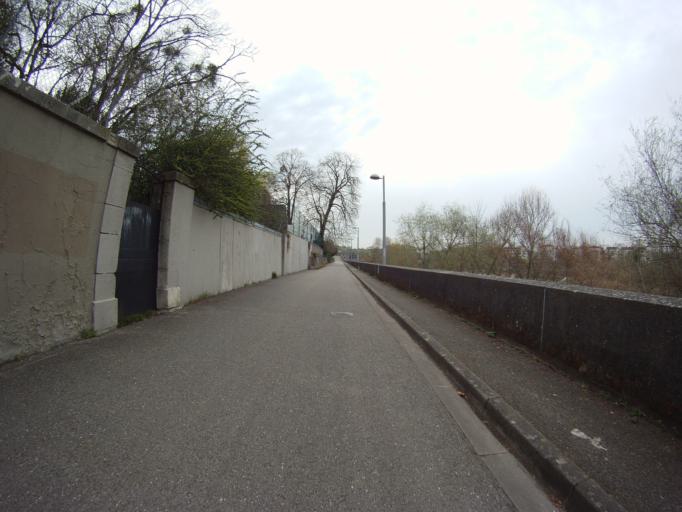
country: FR
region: Lorraine
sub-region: Departement de Meurthe-et-Moselle
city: Saint-Max
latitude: 48.7018
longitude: 6.1962
